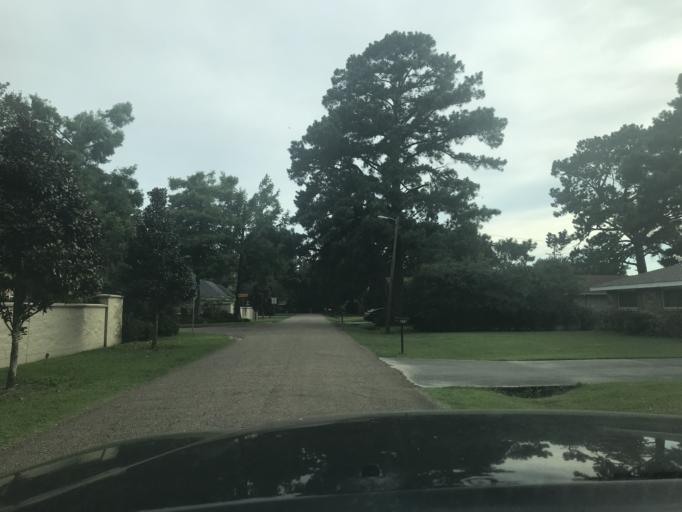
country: US
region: Louisiana
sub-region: Lafayette Parish
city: Lafayette
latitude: 30.2011
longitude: -92.0481
